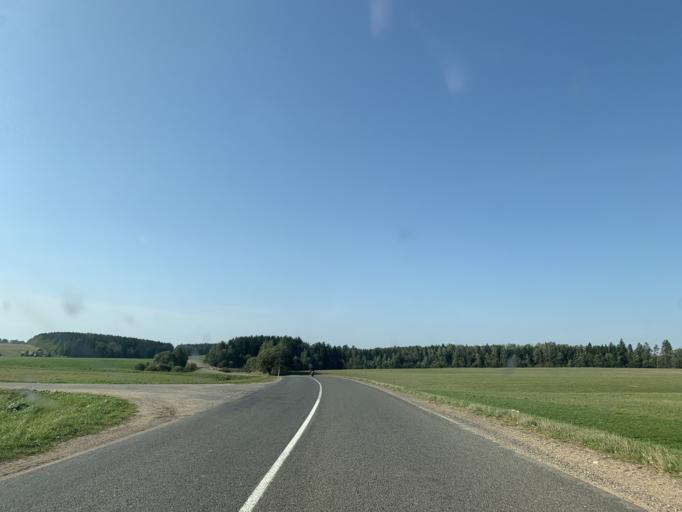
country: BY
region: Minsk
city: Rakaw
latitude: 53.8819
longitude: 26.9608
